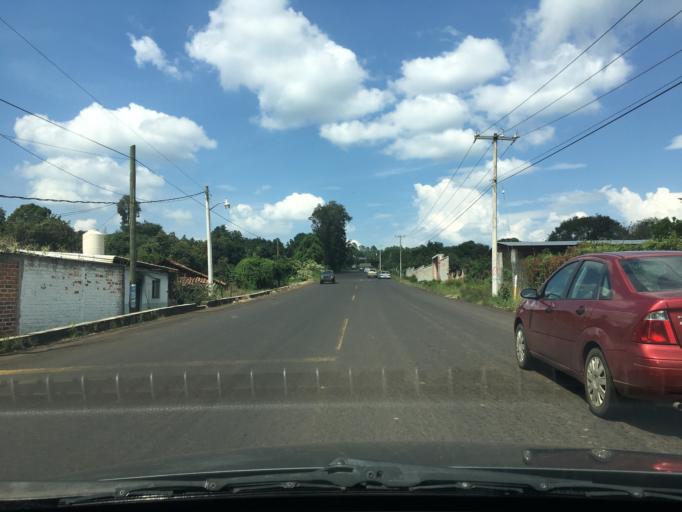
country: MX
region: Michoacan
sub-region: Tingueindin
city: Tingueindin
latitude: 19.8027
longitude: -102.5193
